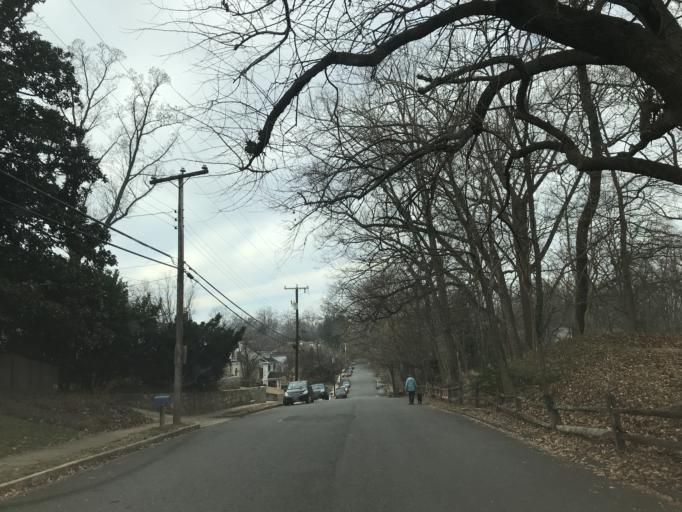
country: US
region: Virginia
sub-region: Arlington County
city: Arlington
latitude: 38.9008
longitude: -77.0909
